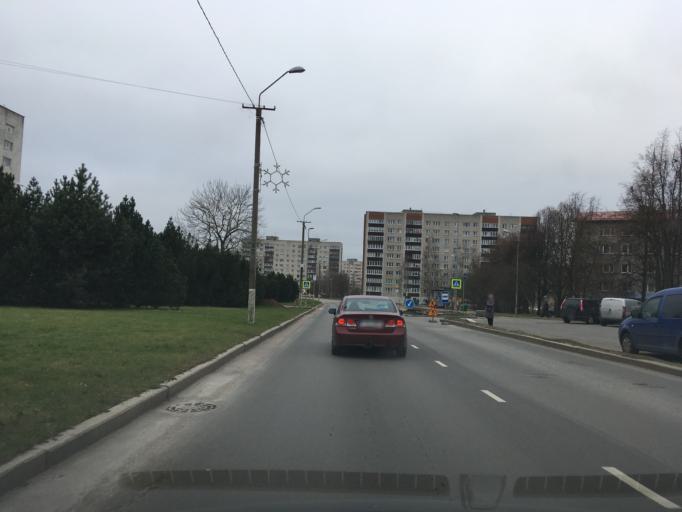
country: EE
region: Ida-Virumaa
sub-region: Narva linn
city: Narva
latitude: 59.3814
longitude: 28.1801
